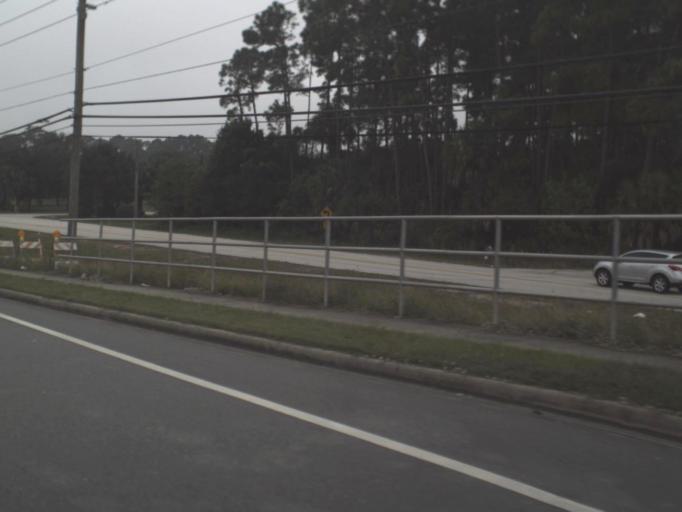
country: US
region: Florida
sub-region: Brevard County
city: June Park
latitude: 28.0473
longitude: -80.6714
